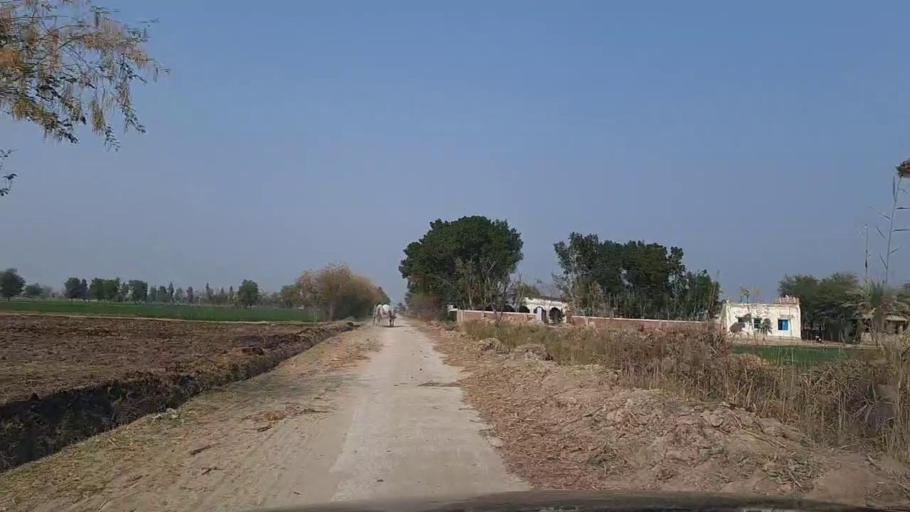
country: PK
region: Sindh
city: Daur
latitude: 26.3976
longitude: 68.4238
